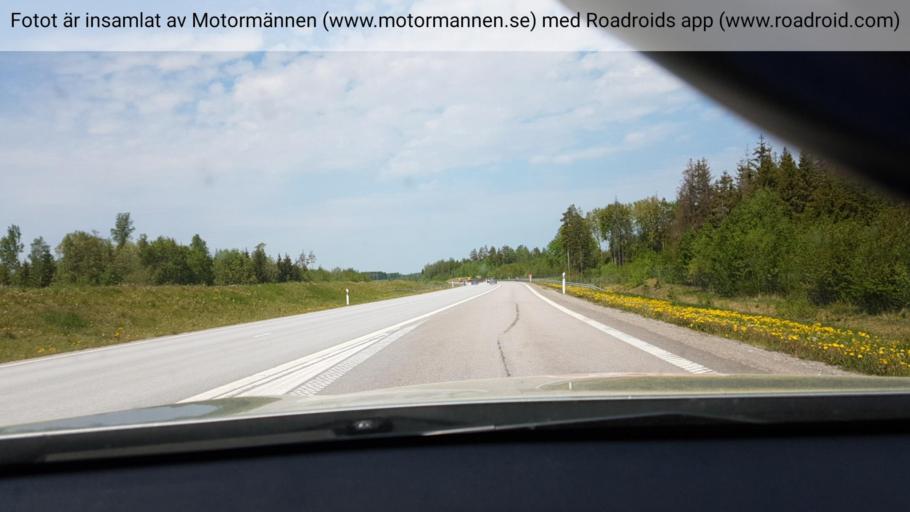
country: SE
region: Uppsala
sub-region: Uppsala Kommun
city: Storvreta
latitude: 59.9932
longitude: 17.6374
